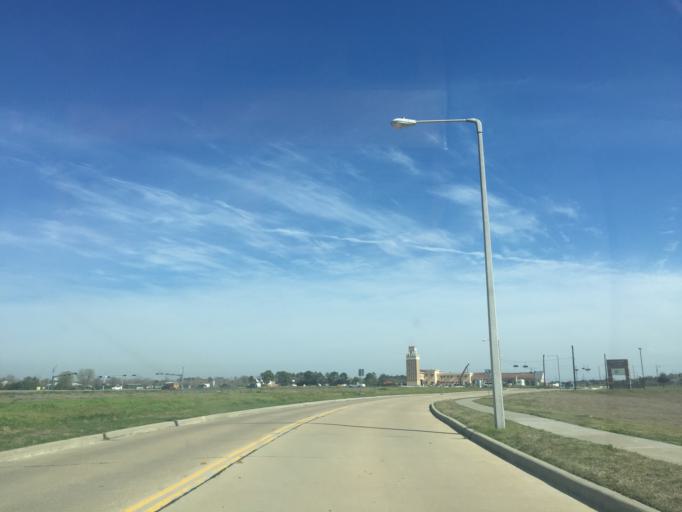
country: US
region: Texas
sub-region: Galveston County
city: Kemah
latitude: 29.5124
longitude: -95.0285
